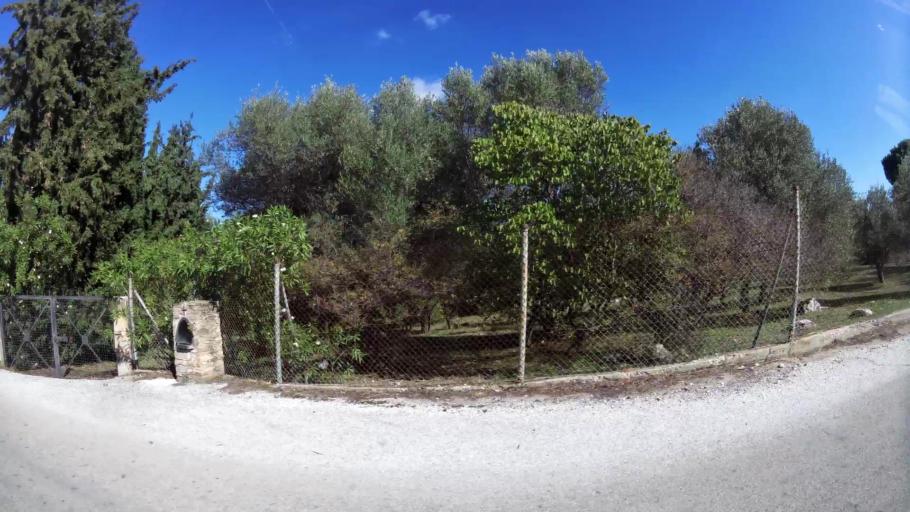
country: GR
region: Attica
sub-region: Nomarchia Anatolikis Attikis
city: Dioni
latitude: 38.0174
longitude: 23.9280
